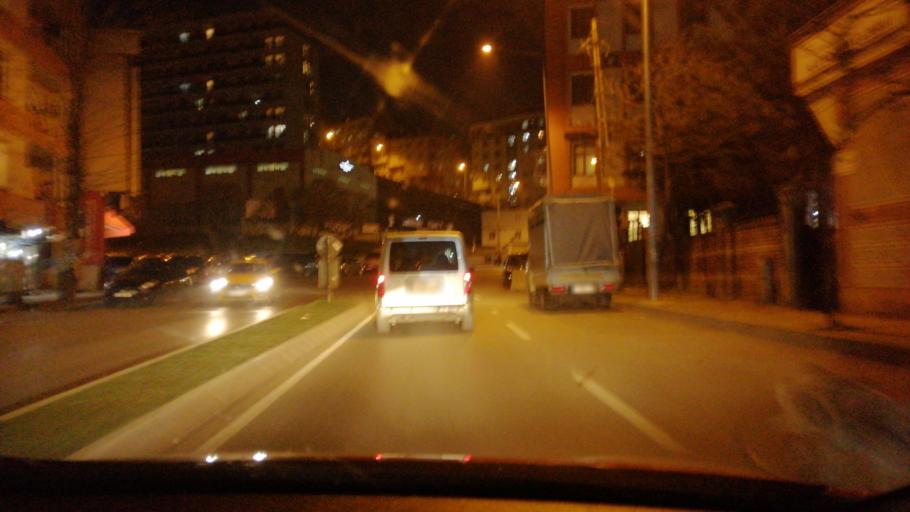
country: TR
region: Istanbul
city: Sisli
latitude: 41.0873
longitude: 28.9732
